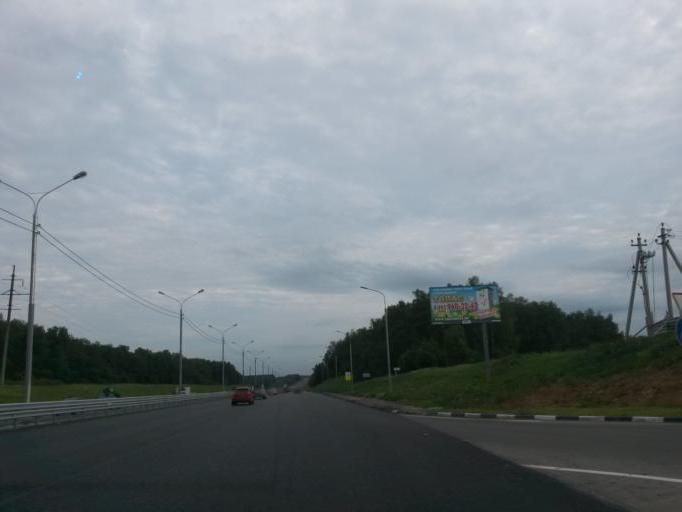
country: RU
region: Moskovskaya
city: Lyubuchany
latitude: 55.2778
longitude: 37.5394
